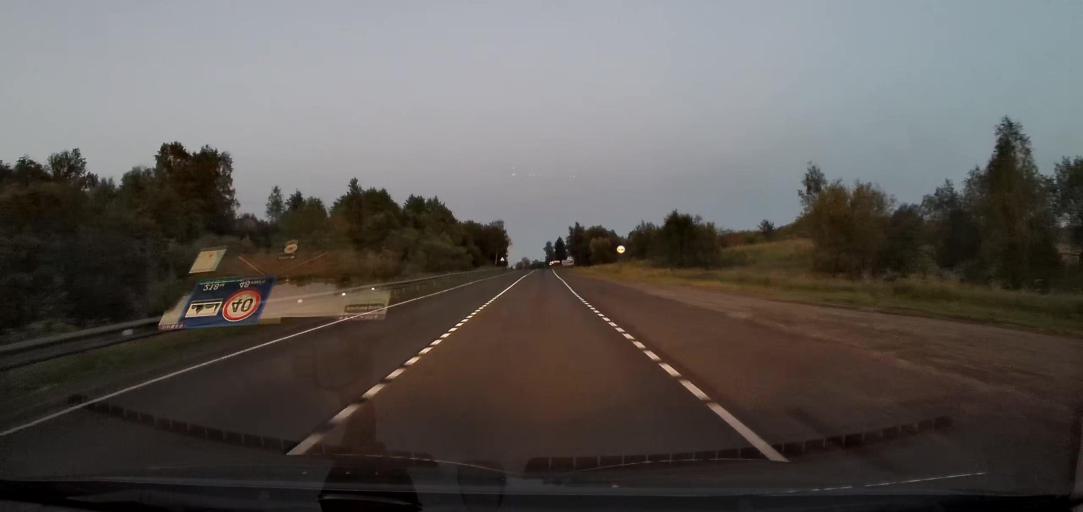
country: RU
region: Arkhangelskaya
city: Uyemskiy
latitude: 64.3848
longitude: 41.0190
